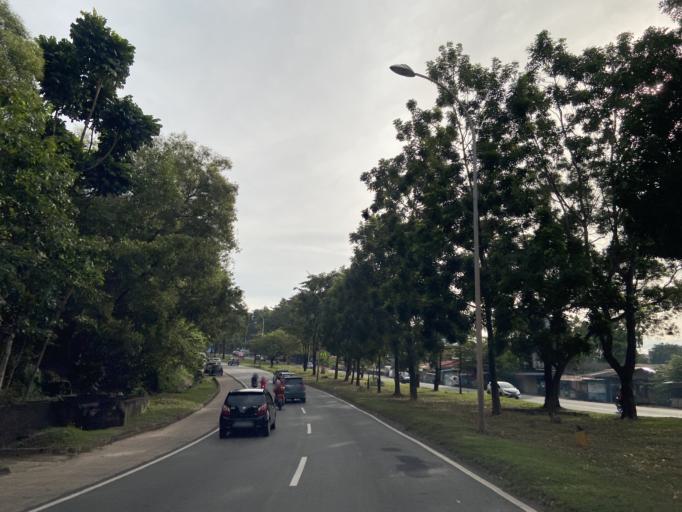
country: SG
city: Singapore
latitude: 1.1339
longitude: 104.0226
